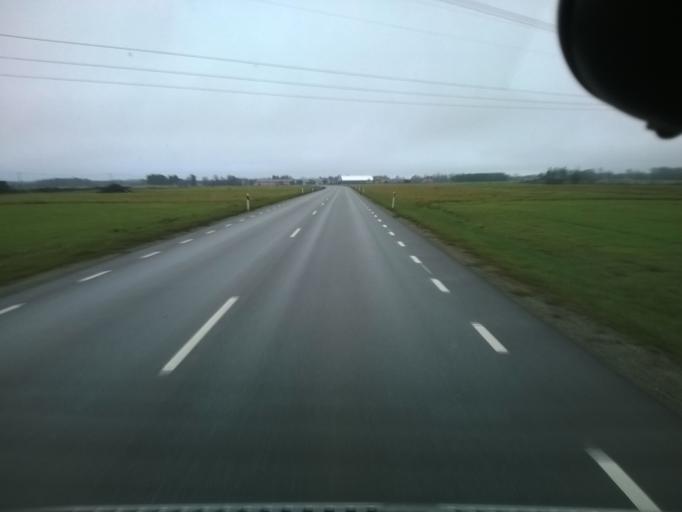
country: EE
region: Harju
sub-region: Saku vald
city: Saku
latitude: 59.2621
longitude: 24.7176
